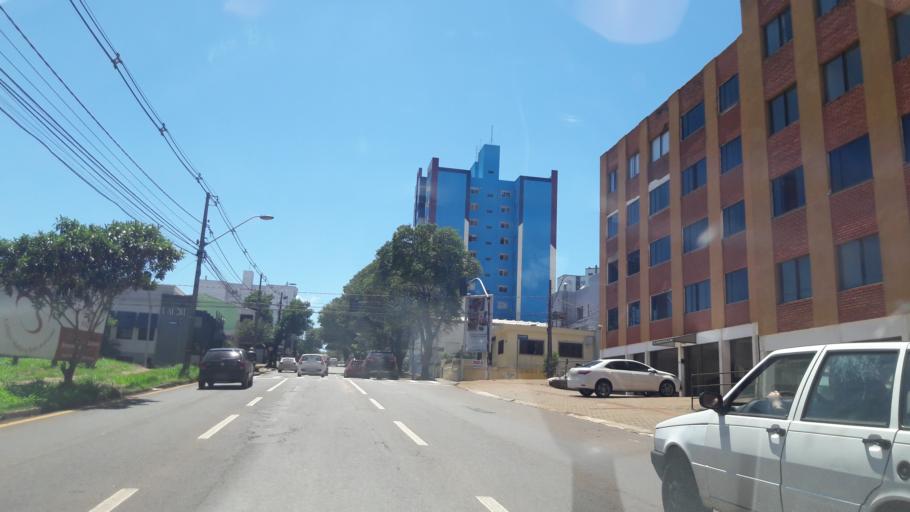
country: BR
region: Parana
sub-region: Cascavel
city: Cascavel
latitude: -24.9517
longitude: -53.4658
